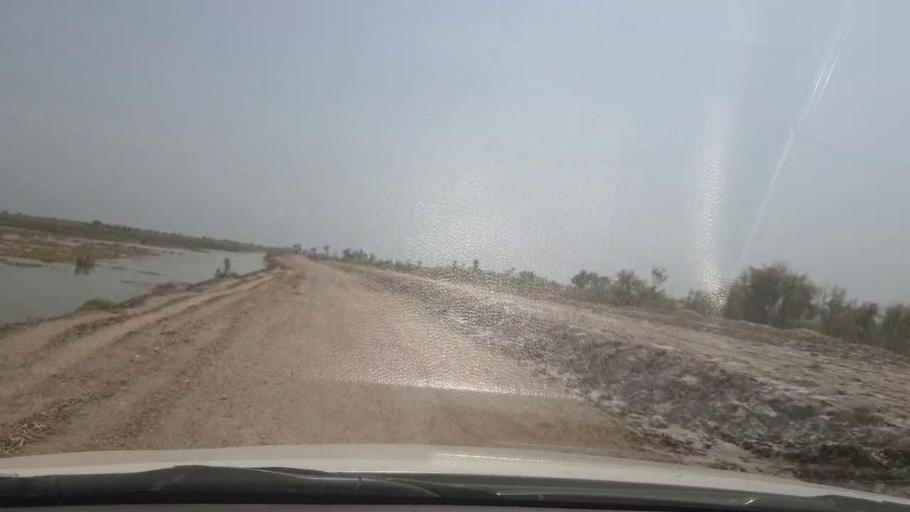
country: PK
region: Sindh
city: Shikarpur
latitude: 28.0352
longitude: 68.5737
